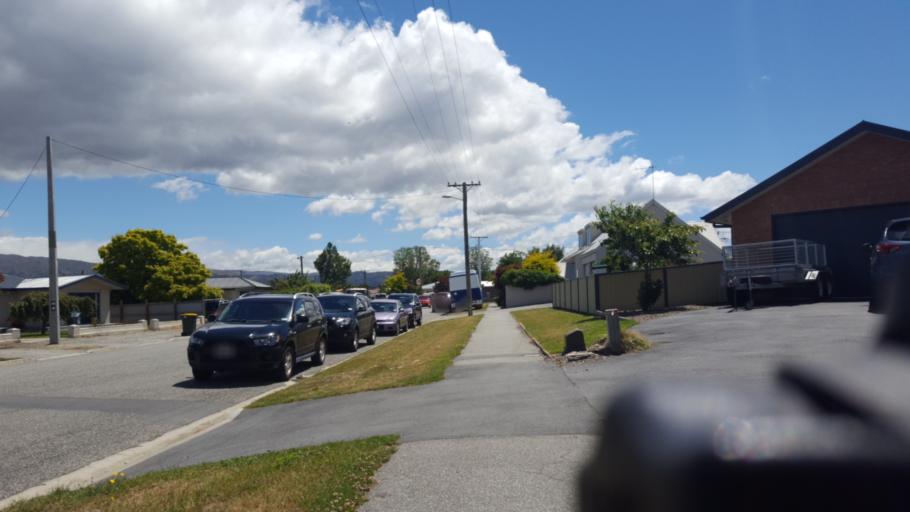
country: NZ
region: Otago
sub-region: Queenstown-Lakes District
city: Wanaka
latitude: -45.2494
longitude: 169.3945
